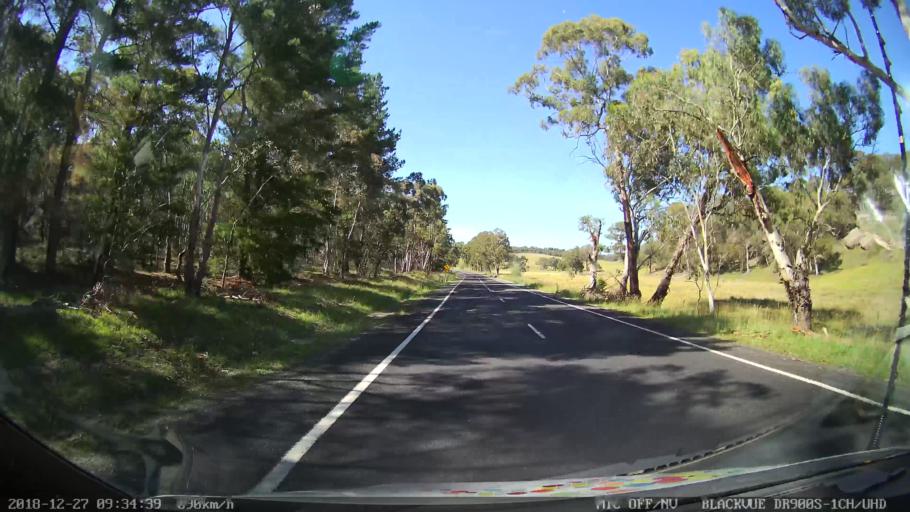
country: AU
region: New South Wales
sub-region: Lithgow
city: Portland
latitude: -33.2288
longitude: 150.0270
